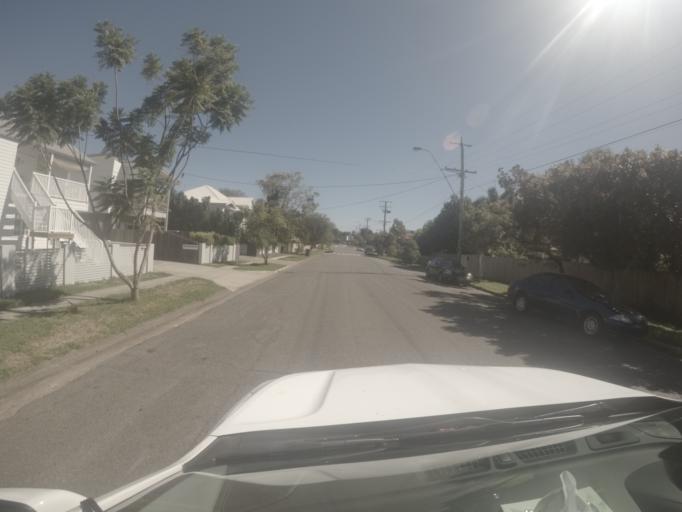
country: AU
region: Queensland
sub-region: Brisbane
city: Rocklea
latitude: -27.5342
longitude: 152.9864
